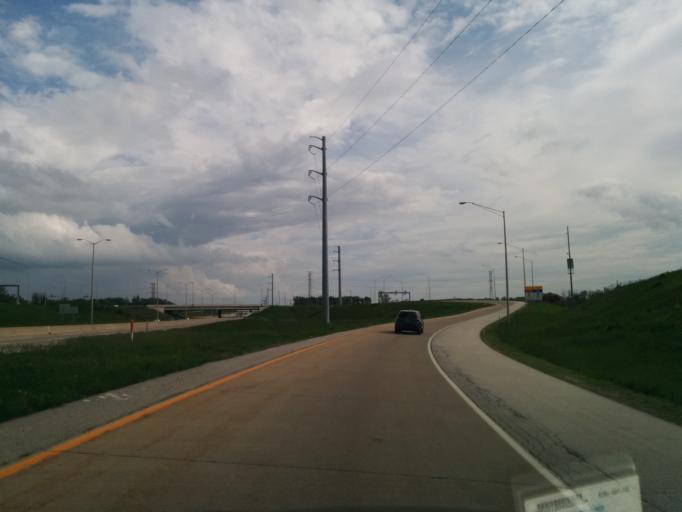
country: US
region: Illinois
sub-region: Cook County
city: Lemont
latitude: 41.6388
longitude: -88.0128
